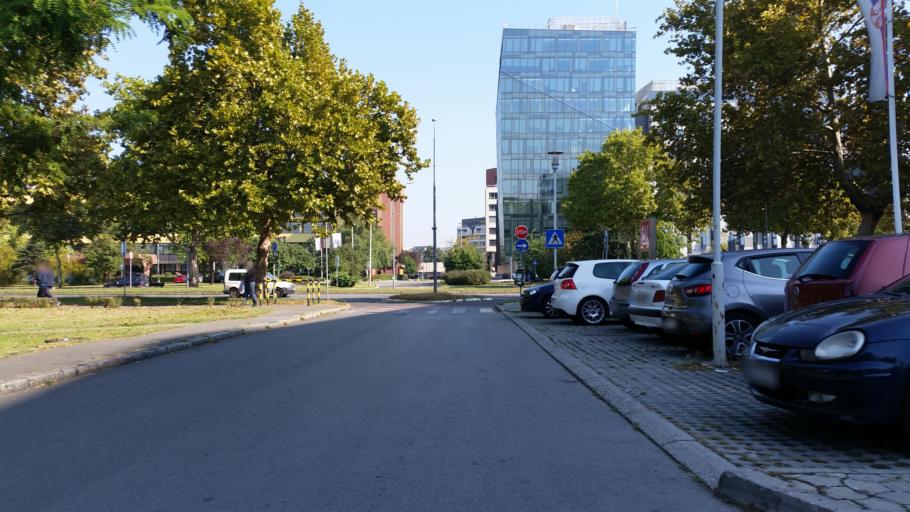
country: RS
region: Central Serbia
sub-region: Belgrade
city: Novi Beograd
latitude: 44.8228
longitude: 20.4150
